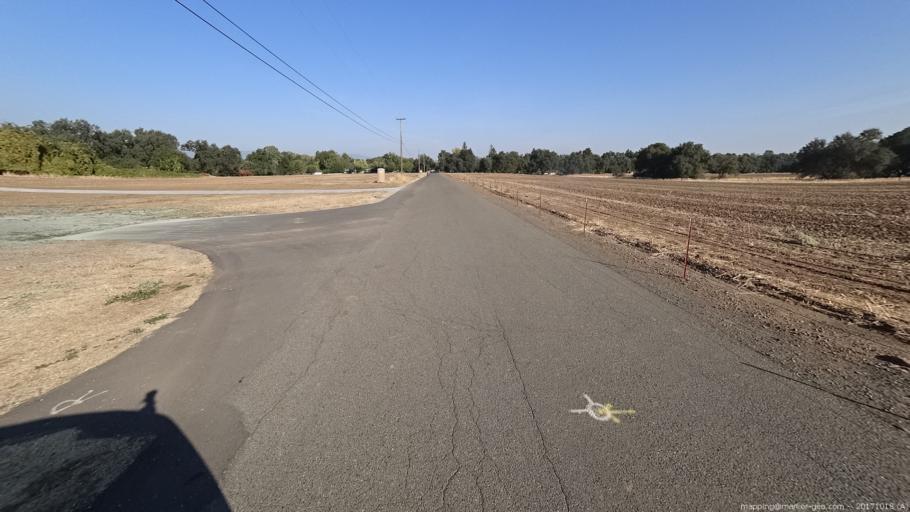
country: US
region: California
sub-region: Shasta County
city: Redding
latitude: 40.5587
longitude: -122.3698
